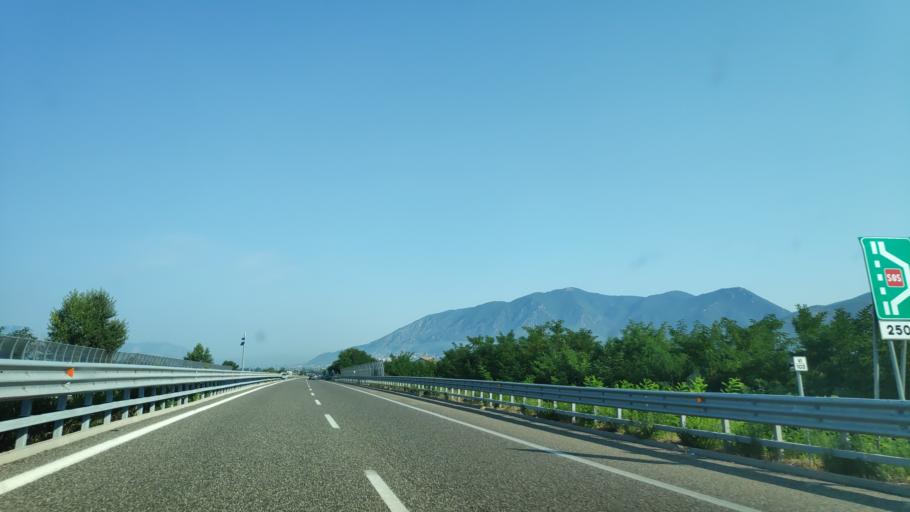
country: IT
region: Campania
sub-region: Provincia di Salerno
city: Padula
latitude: 40.3379
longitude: 15.6259
